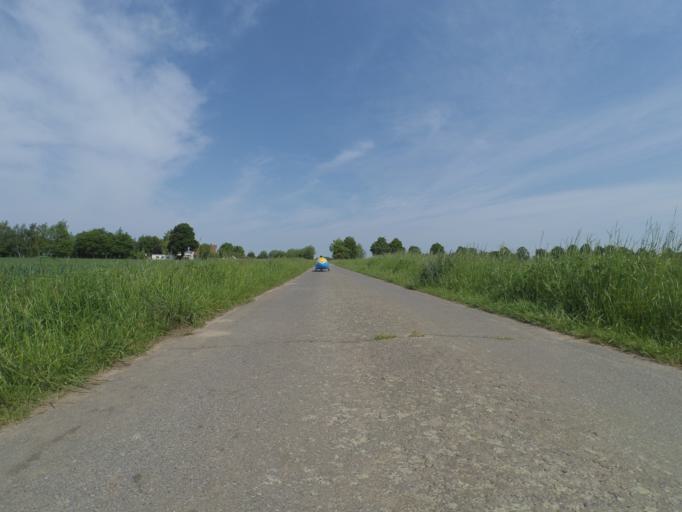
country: DE
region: Lower Saxony
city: Hohenhameln
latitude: 52.2672
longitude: 10.0406
